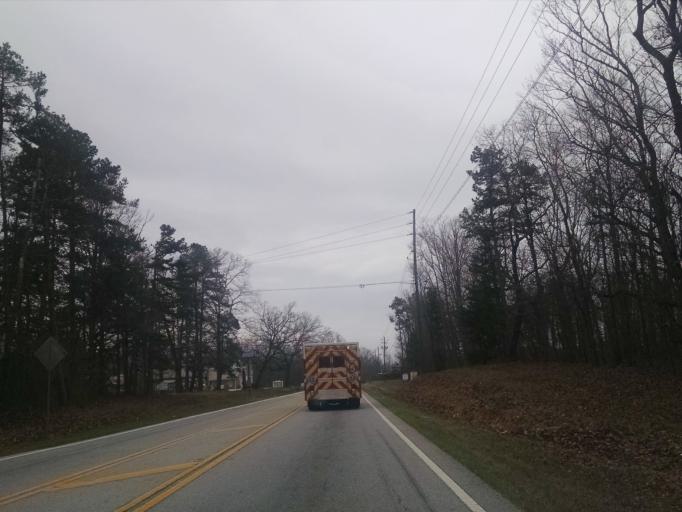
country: US
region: Georgia
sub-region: Hall County
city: Oakwood
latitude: 34.1984
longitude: -83.8875
